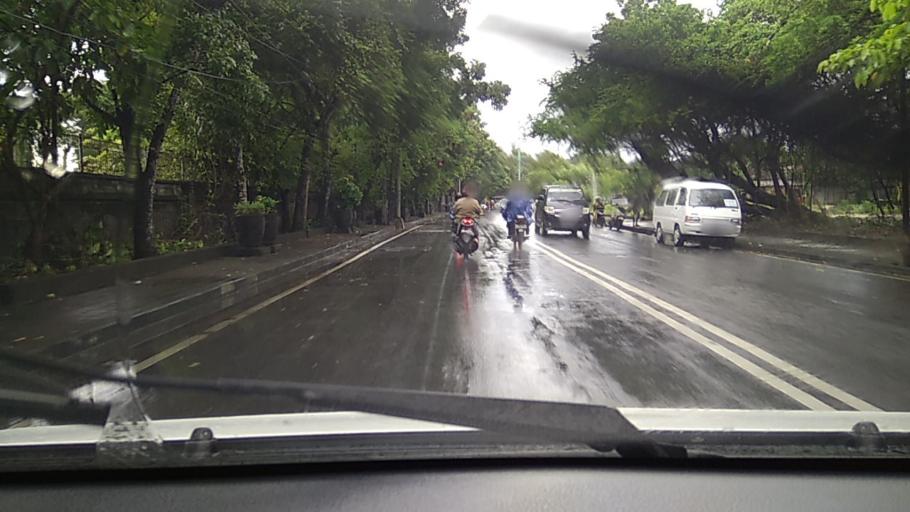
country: ID
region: Bali
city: Bualu
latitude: -8.7895
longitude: 115.2245
